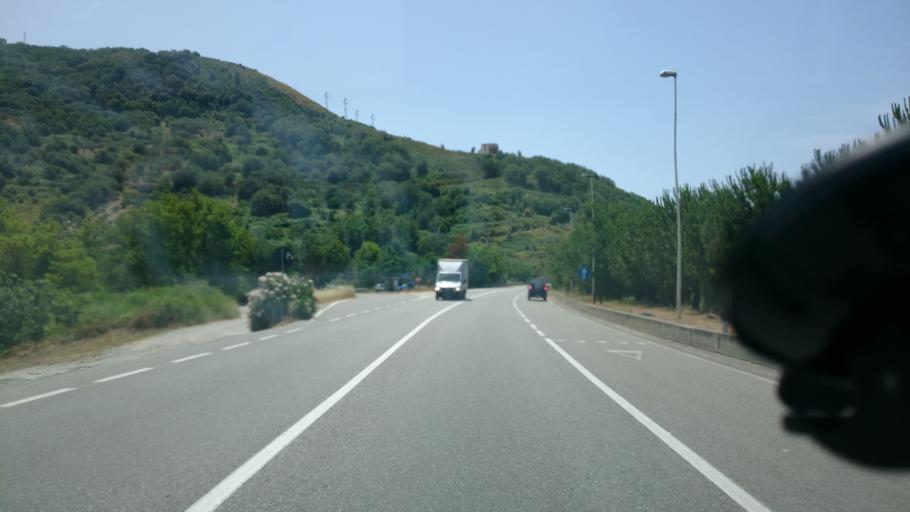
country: IT
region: Calabria
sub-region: Provincia di Cosenza
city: Cittadella del Capo
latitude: 39.5887
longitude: 15.8695
